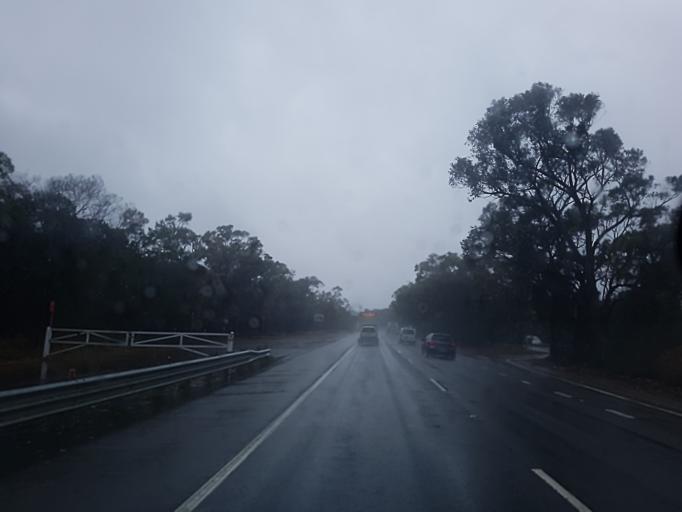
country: AU
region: New South Wales
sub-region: Warringah
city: Davidson
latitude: -33.7087
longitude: 151.1983
